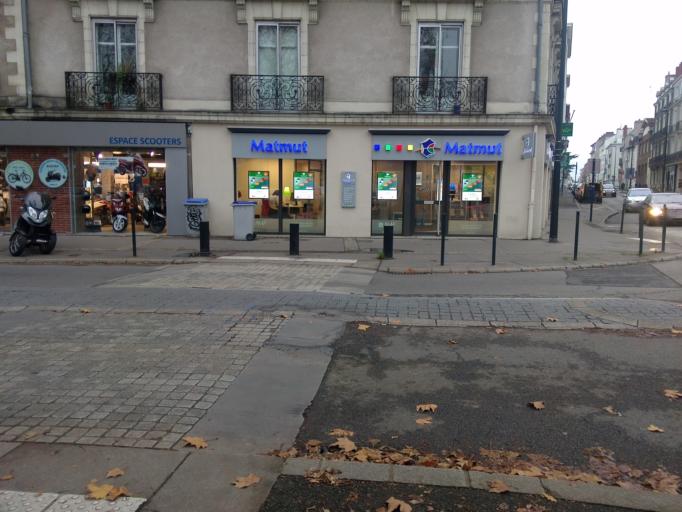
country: FR
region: Pays de la Loire
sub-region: Departement de la Loire-Atlantique
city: Nantes
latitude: 47.2211
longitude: -1.5631
